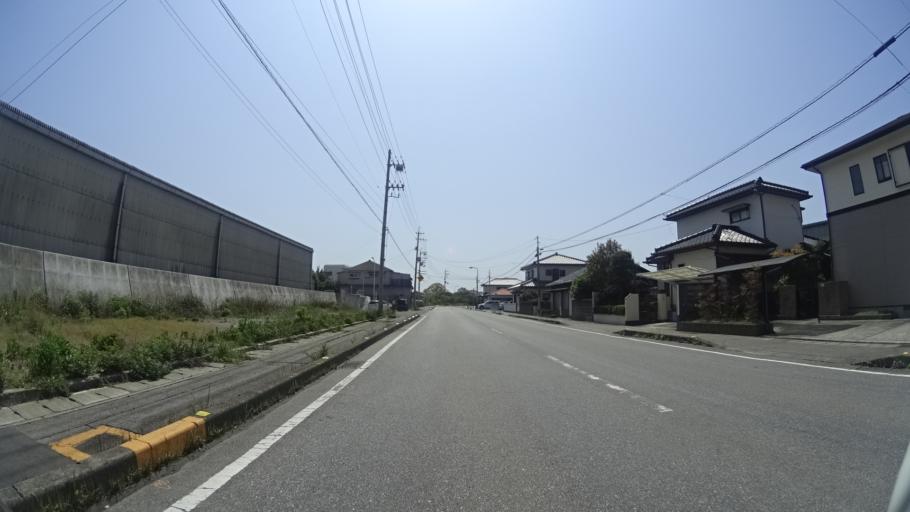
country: JP
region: Tokushima
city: Narutocho-mitsuishi
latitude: 34.1877
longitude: 134.6145
